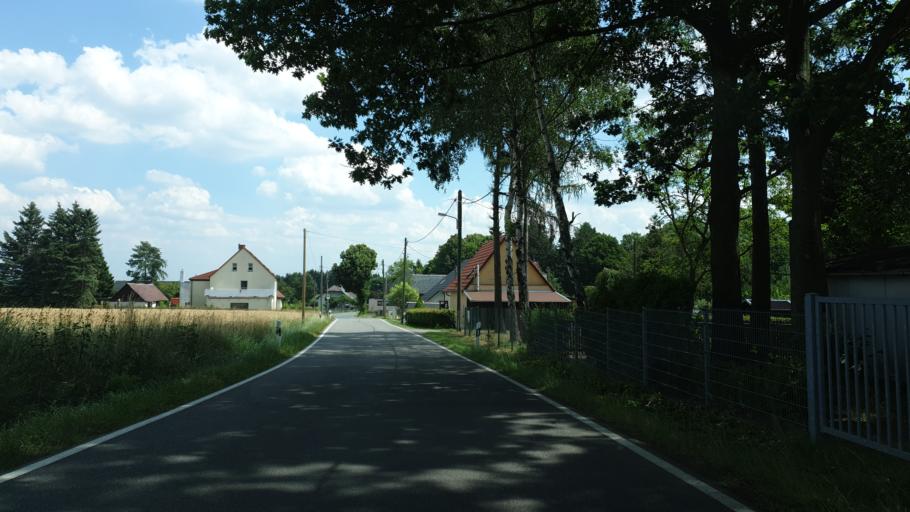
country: DE
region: Saxony
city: Kirchberg
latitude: 50.8026
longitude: 12.7714
